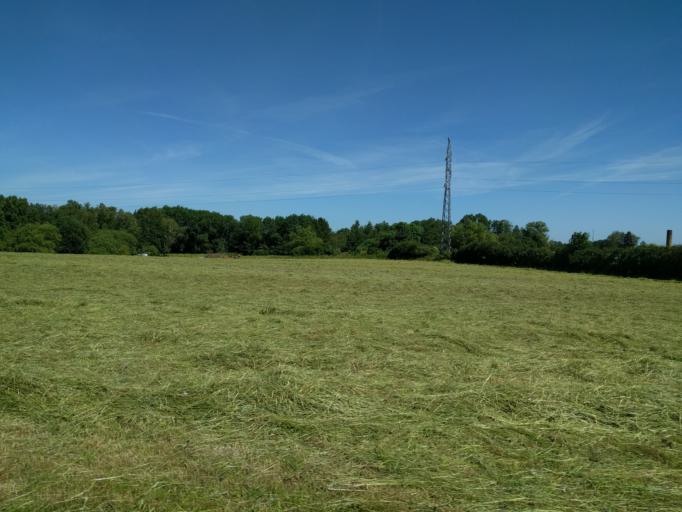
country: DK
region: South Denmark
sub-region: Kerteminde Kommune
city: Langeskov
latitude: 55.3431
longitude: 10.5865
